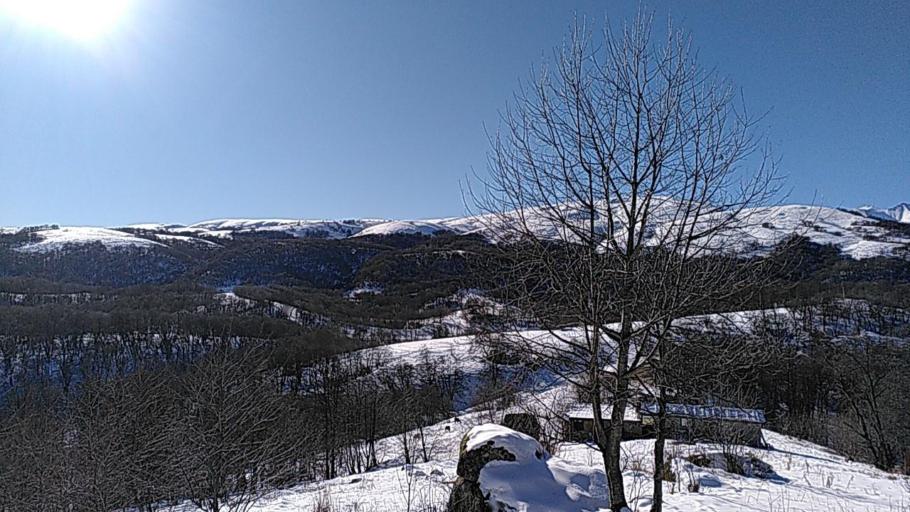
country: RU
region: Kabardino-Balkariya
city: Belaya Rechka
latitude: 43.3577
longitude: 43.4028
